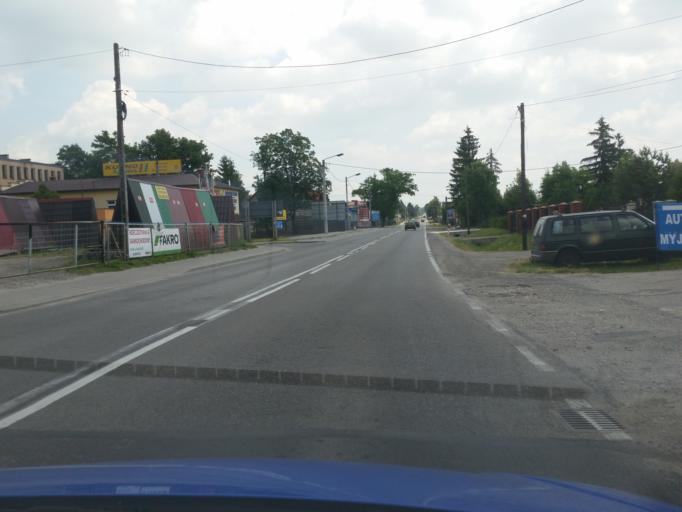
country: PL
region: Lesser Poland Voivodeship
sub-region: Powiat miechowski
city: Miechow
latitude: 50.3569
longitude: 20.0450
